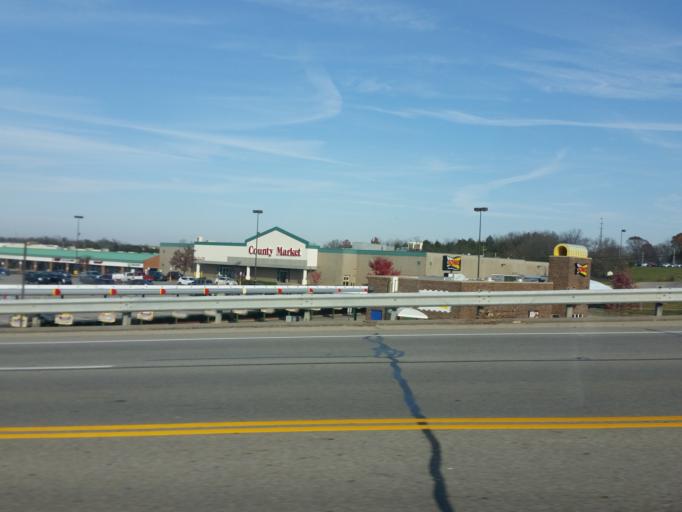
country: US
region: Kentucky
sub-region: Campbell County
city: Alexandria
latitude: 38.9835
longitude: -84.4002
